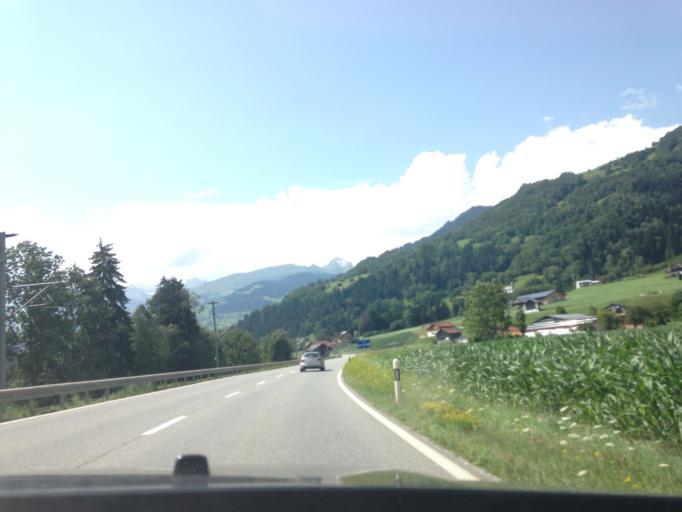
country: CH
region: Grisons
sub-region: Surselva District
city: Ilanz
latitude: 46.7734
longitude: 9.1816
